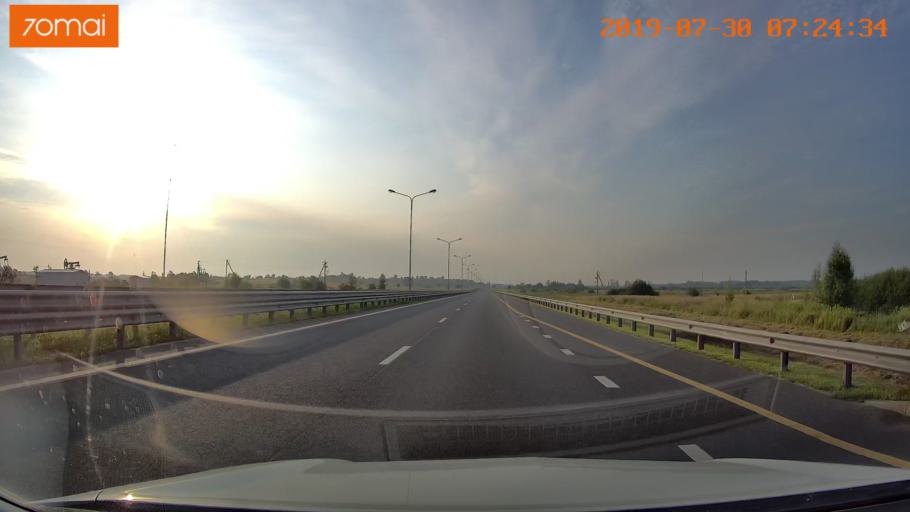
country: RU
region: Kaliningrad
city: Bol'shoe Isakovo
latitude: 54.6928
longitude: 20.8153
